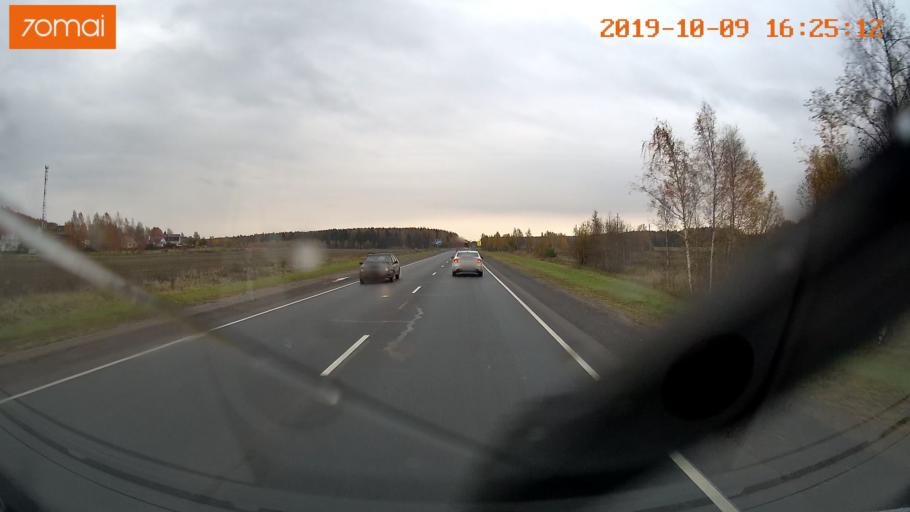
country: RU
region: Kostroma
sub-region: Kostromskoy Rayon
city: Kostroma
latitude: 57.6445
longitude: 40.9178
